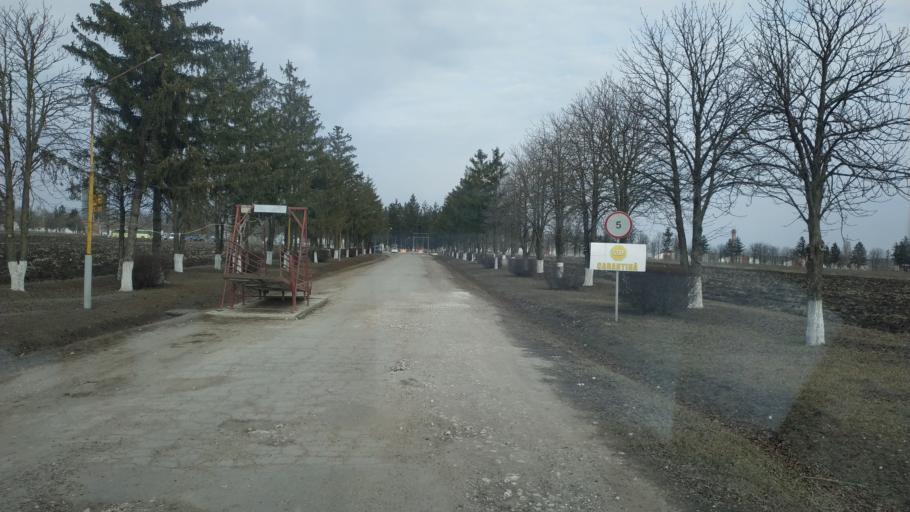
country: MD
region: Chisinau
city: Vadul lui Voda
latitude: 46.9935
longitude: 29.1047
